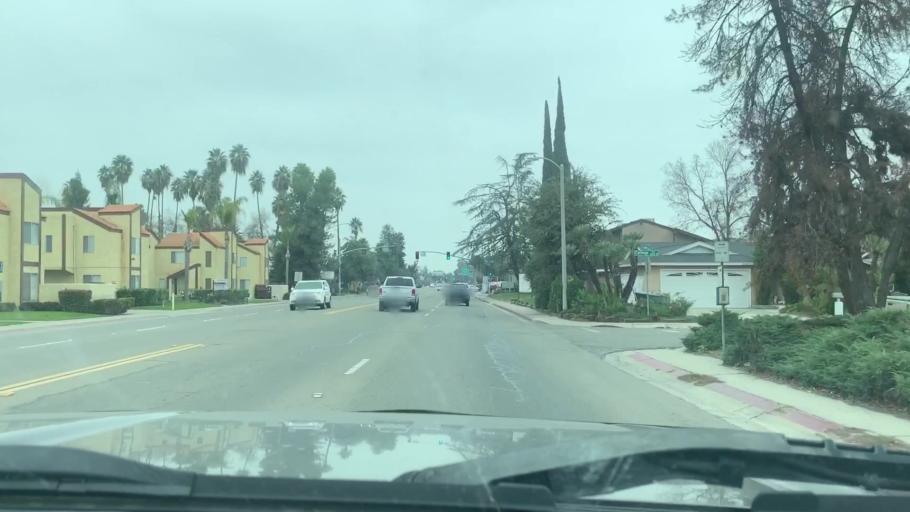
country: US
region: California
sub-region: Tulare County
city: Visalia
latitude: 36.3231
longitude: -119.3317
